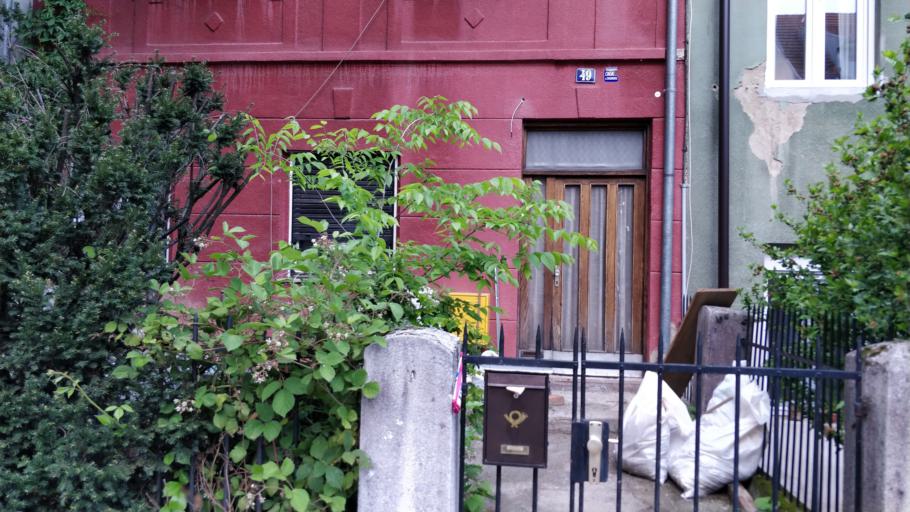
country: HR
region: Grad Zagreb
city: Zagreb
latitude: 45.8131
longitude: 16.0072
